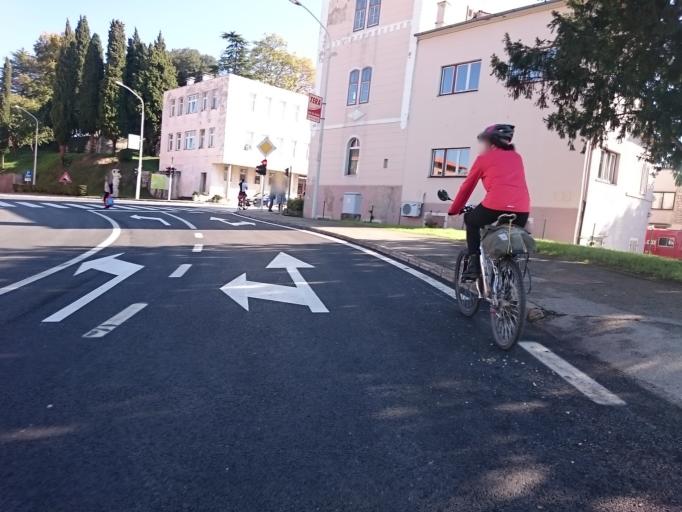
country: HR
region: Istarska
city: Buje
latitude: 45.4082
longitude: 13.6584
